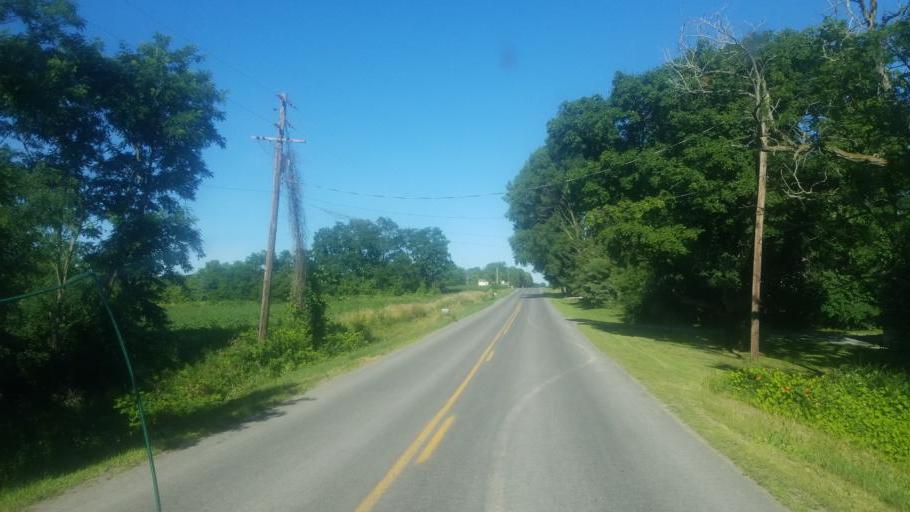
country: US
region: New York
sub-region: Ontario County
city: Canandaigua
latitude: 42.8360
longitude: -77.1919
